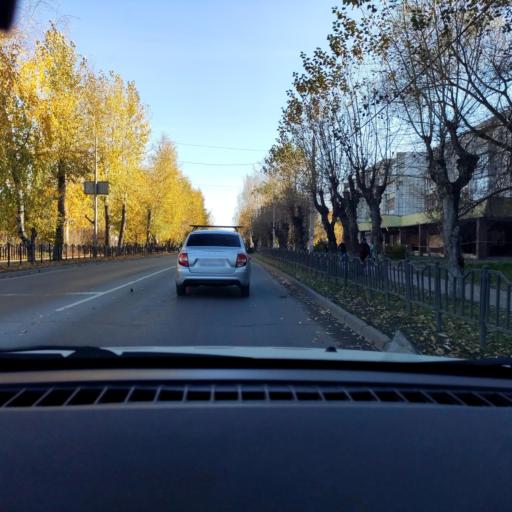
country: RU
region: Perm
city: Perm
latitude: 58.1063
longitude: 56.3820
